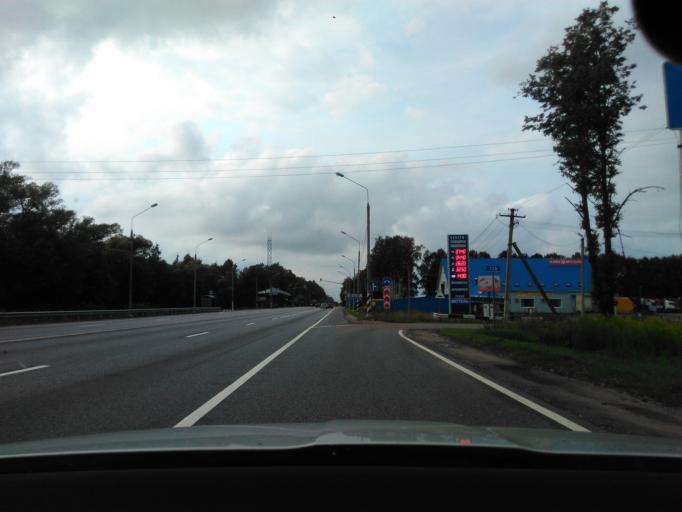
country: RU
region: Tverskaya
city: Zavidovo
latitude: 56.5543
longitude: 36.5123
